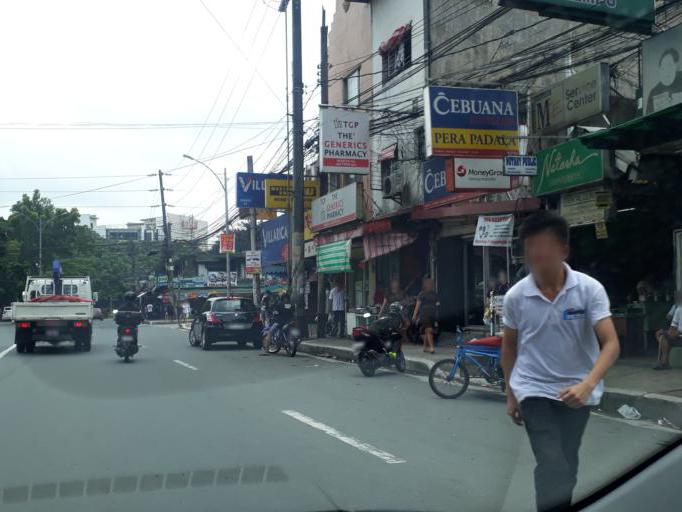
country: PH
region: Calabarzon
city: Del Monte
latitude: 14.6328
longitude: 121.0204
